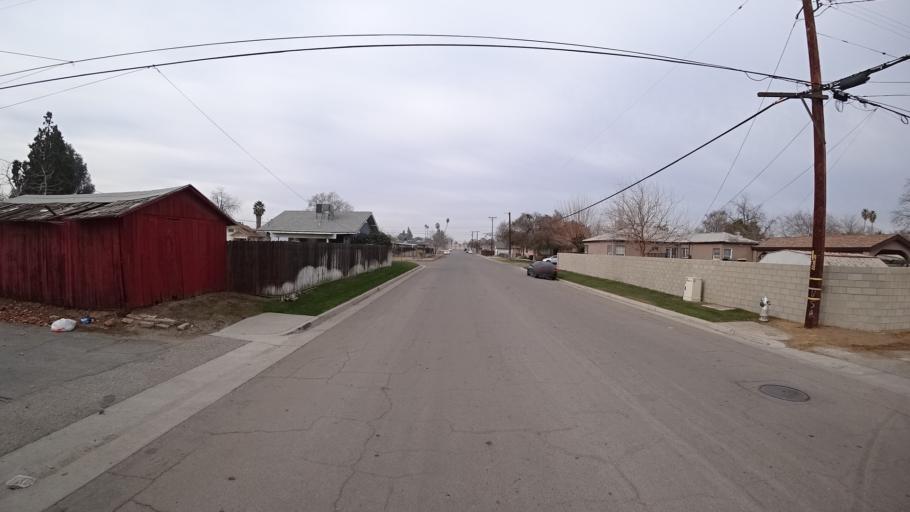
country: US
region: California
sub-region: Kern County
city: Bakersfield
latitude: 35.3633
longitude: -119.0355
